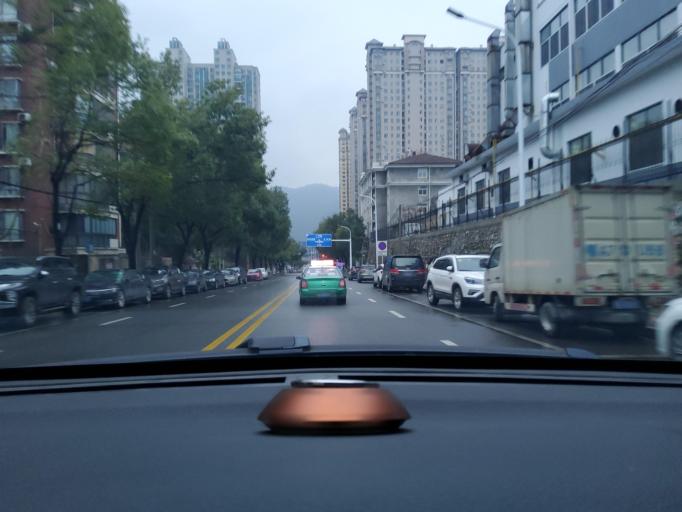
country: CN
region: Hubei
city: Tuanchengshan
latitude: 30.1910
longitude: 115.0275
